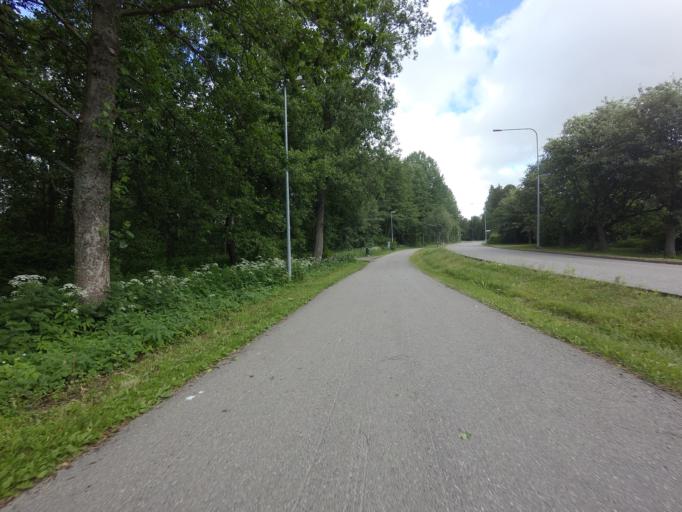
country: FI
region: Uusimaa
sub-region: Helsinki
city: Espoo
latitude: 60.1353
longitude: 24.6622
